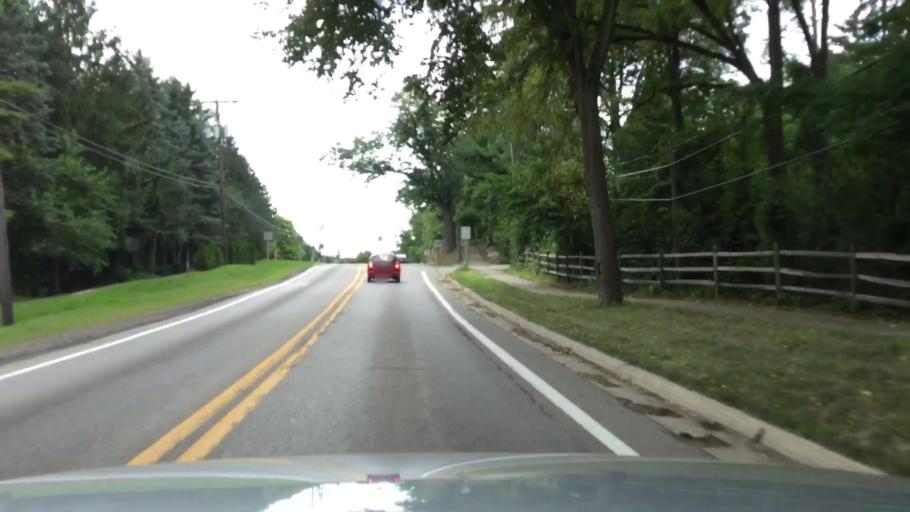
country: US
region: Michigan
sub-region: Oakland County
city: Bloomfield Hills
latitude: 42.5916
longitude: -83.2079
